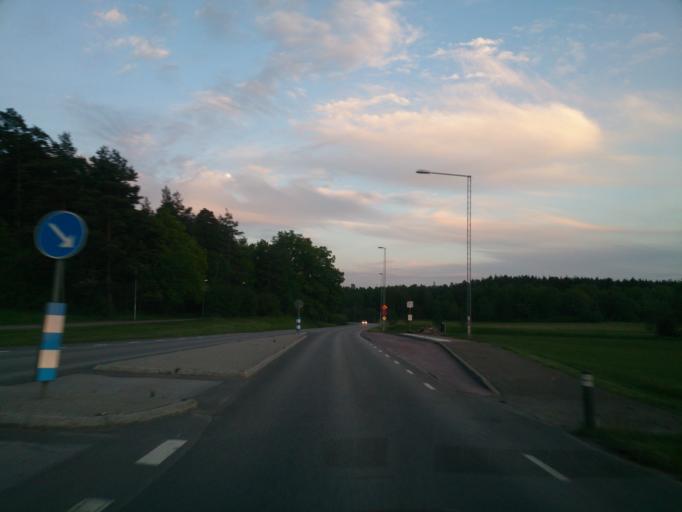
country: SE
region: OEstergoetland
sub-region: Linkopings Kommun
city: Linkoping
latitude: 58.3800
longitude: 15.6346
